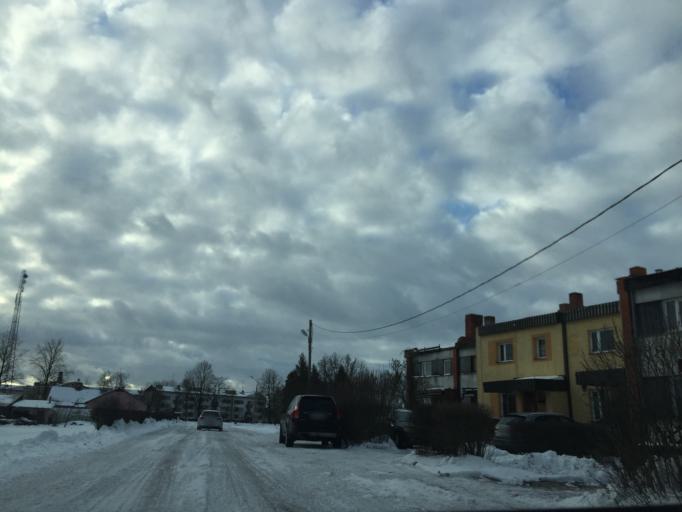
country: LV
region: Lielvarde
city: Lielvarde
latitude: 56.6330
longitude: 24.7534
